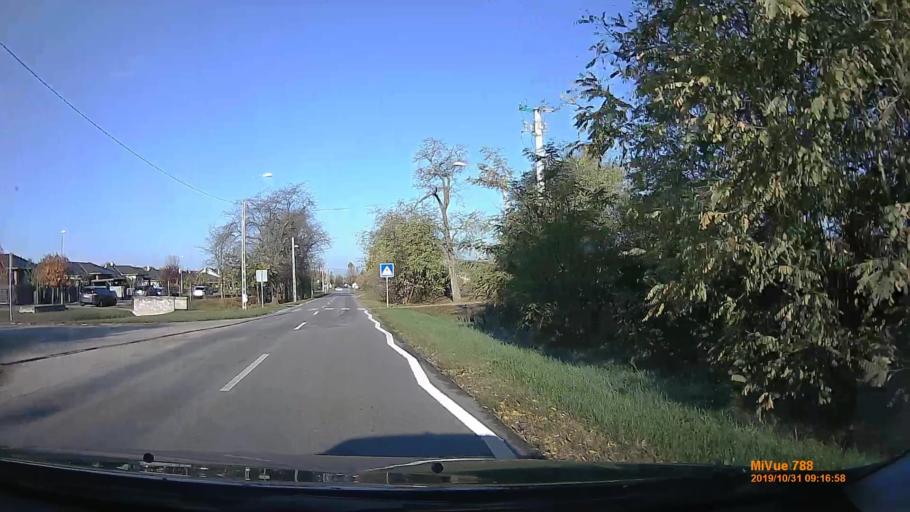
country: HU
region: Pest
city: Peteri
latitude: 47.4057
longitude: 19.4103
